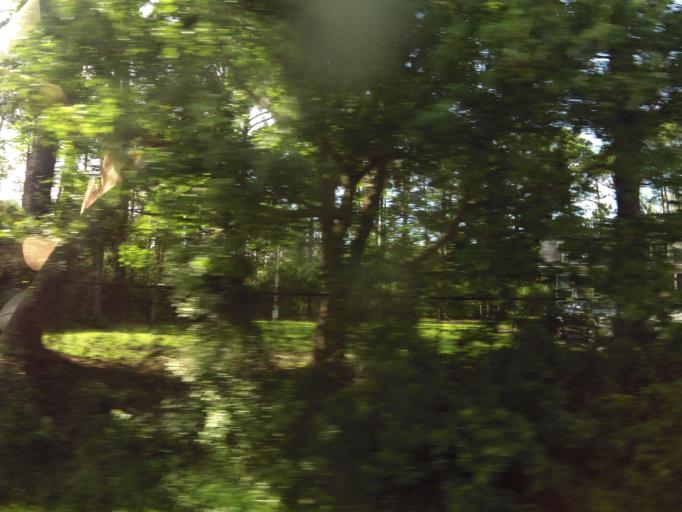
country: US
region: Florida
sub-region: Nassau County
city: Fernandina Beach
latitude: 30.5123
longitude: -81.4715
